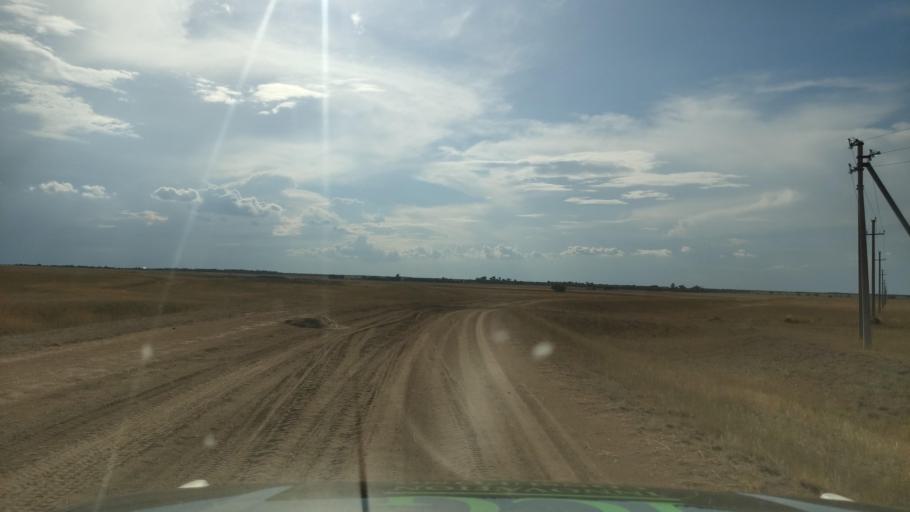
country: KZ
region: Pavlodar
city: Pavlodar
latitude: 52.5129
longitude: 77.4657
